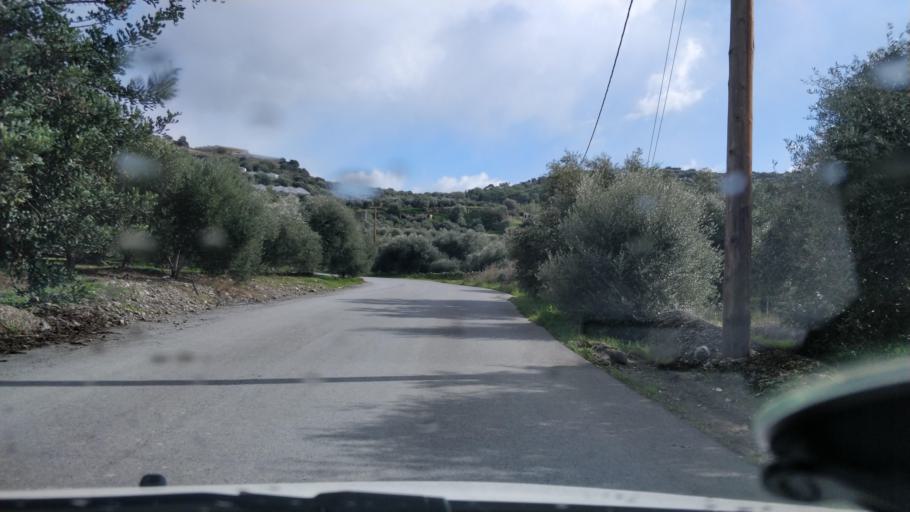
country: GR
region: Crete
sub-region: Nomos Lasithiou
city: Gra Liyia
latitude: 34.9956
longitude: 25.5048
